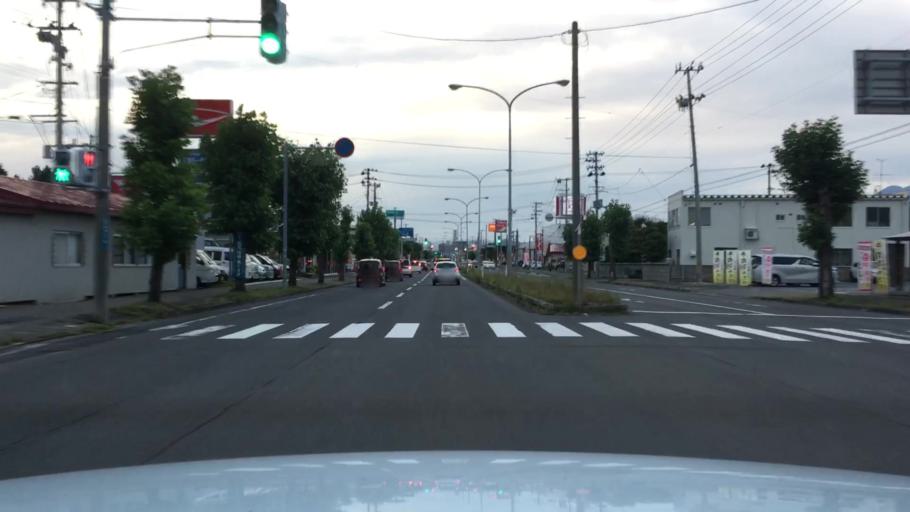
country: JP
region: Aomori
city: Hirosaki
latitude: 40.5963
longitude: 140.5016
